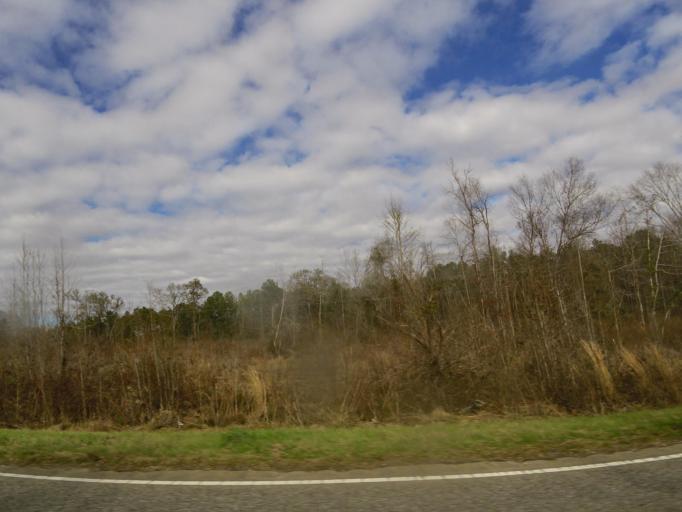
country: US
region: Alabama
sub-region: Barbour County
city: Eufaula
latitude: 31.9725
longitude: -85.2259
